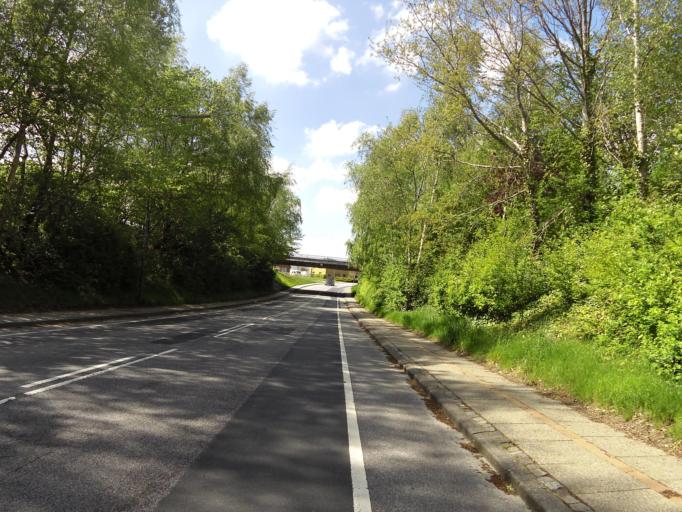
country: DK
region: South Denmark
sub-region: Tonder Kommune
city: Toftlund
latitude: 55.1856
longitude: 9.0681
